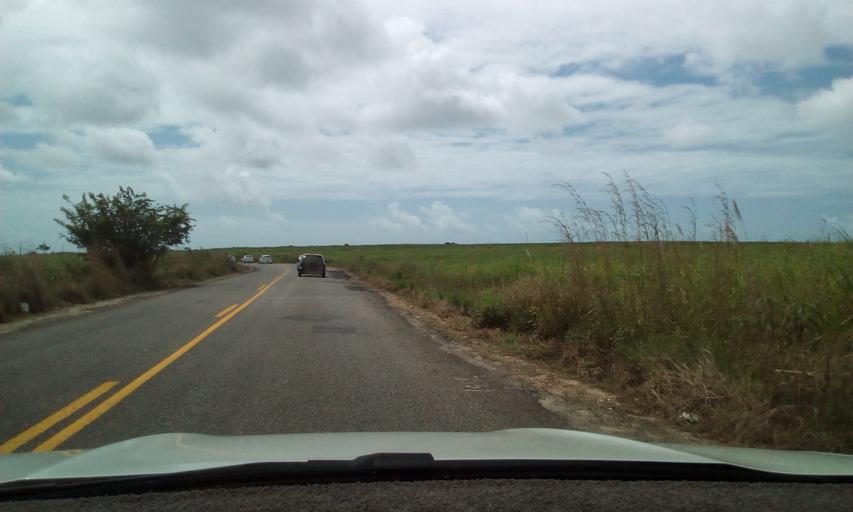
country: BR
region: Paraiba
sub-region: Rio Tinto
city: Rio Tinto
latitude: -6.7653
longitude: -35.0028
